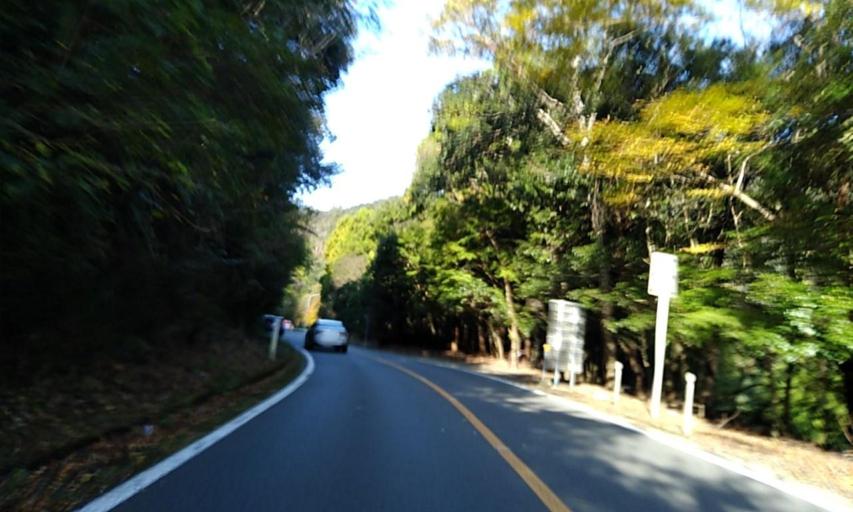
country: JP
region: Mie
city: Ise
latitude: 34.4565
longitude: 136.7389
